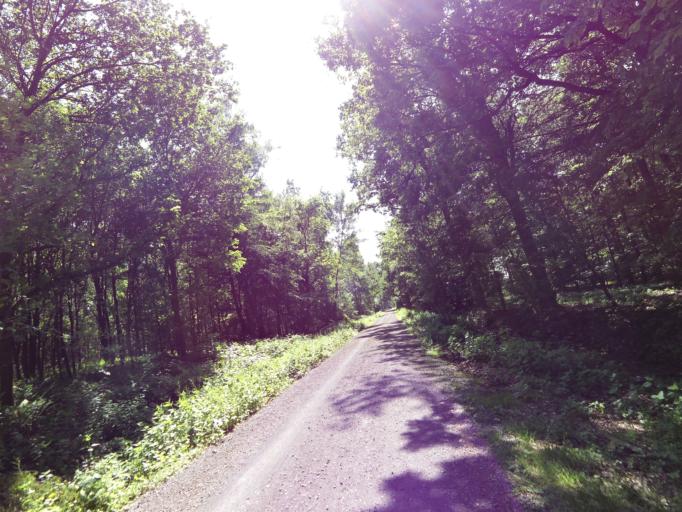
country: DE
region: North Rhine-Westphalia
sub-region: Regierungsbezirk Koln
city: Wachtberg
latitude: 50.6816
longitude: 7.1123
